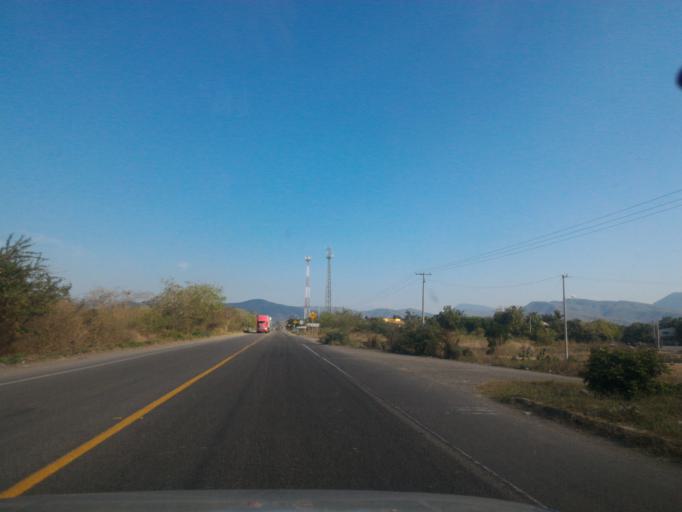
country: MX
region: Michoacan
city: Coahuayana Viejo
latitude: 18.7464
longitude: -103.7241
